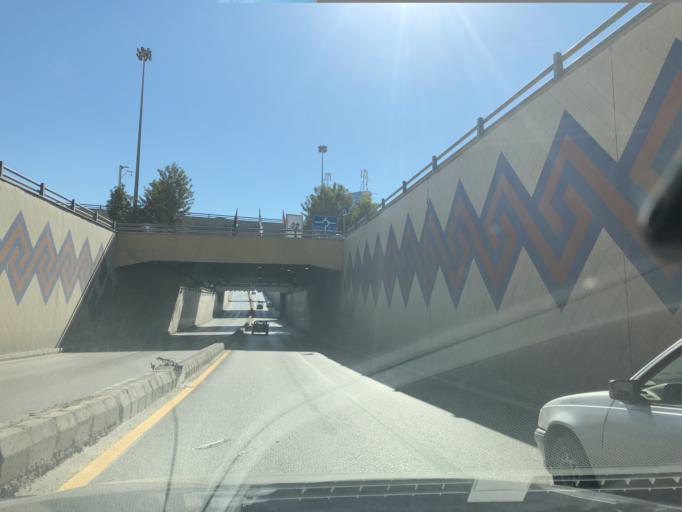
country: JO
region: Amman
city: Wadi as Sir
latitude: 31.9748
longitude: 35.8642
